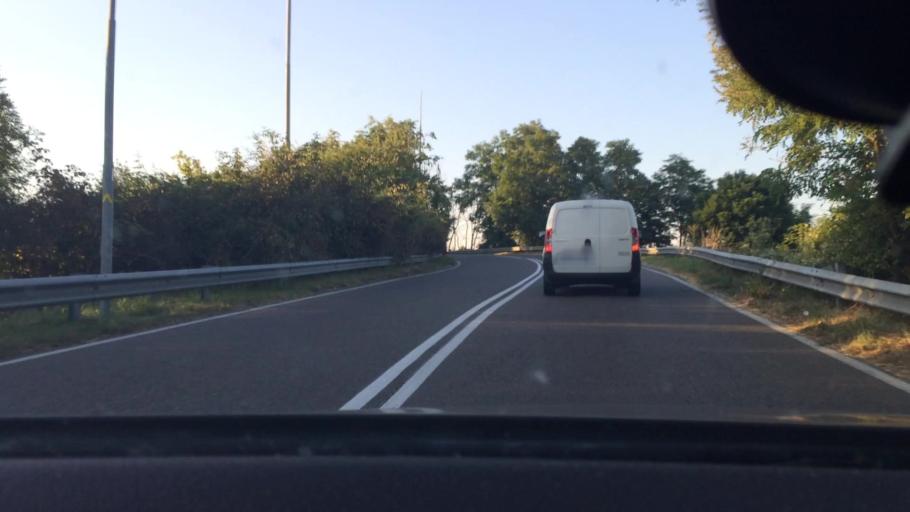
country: IT
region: Lombardy
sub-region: Citta metropolitana di Milano
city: Rescaldina
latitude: 45.6222
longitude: 8.9604
